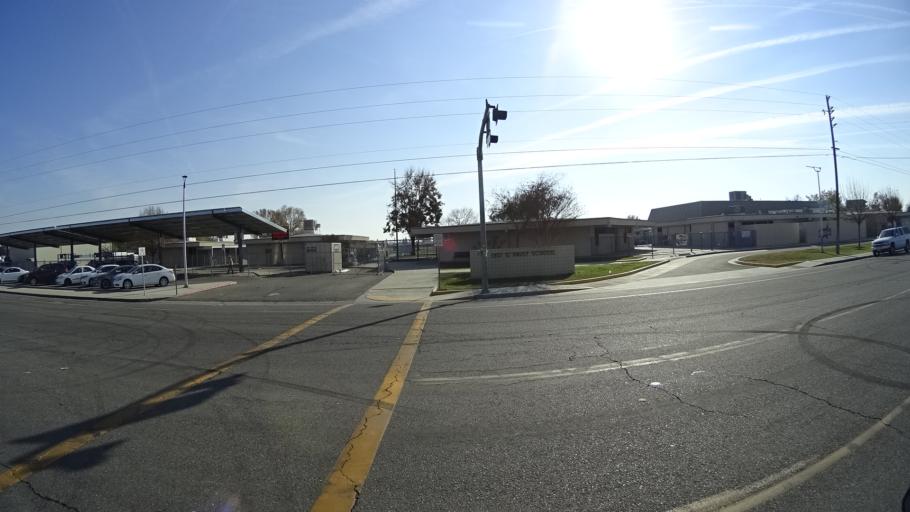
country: US
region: California
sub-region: Kern County
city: Bakersfield
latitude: 35.3250
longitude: -119.0062
